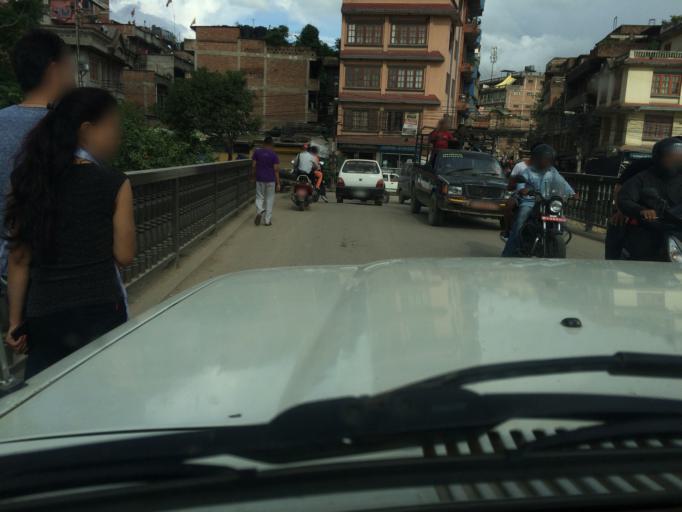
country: NP
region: Central Region
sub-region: Bagmati Zone
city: Kathmandu
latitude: 27.7095
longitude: 85.3029
